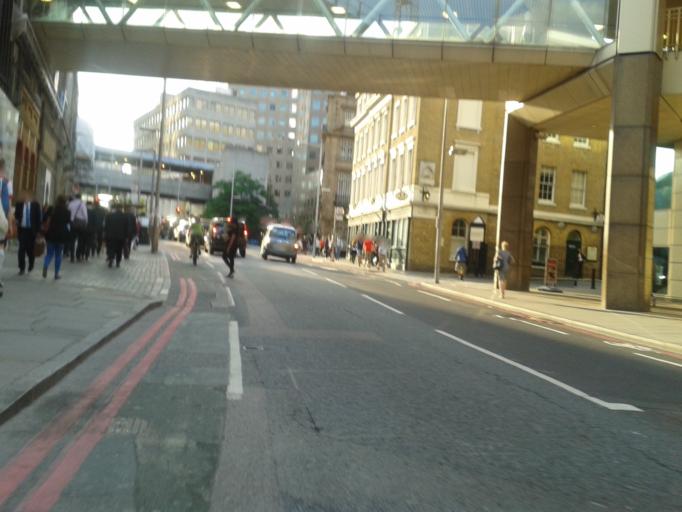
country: GB
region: England
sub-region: Greater London
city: City of London
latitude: 51.5056
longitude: -0.0852
